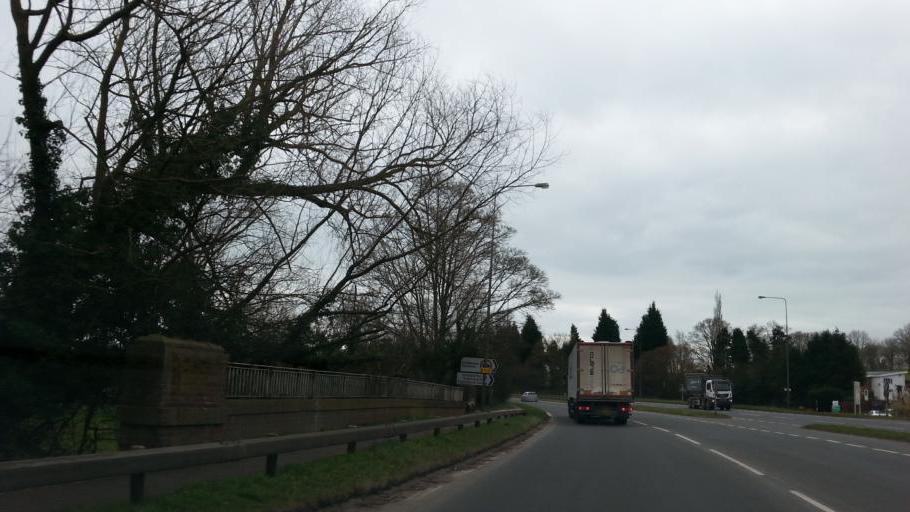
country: GB
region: England
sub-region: Staffordshire
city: Stone
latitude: 52.9043
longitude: -2.1610
